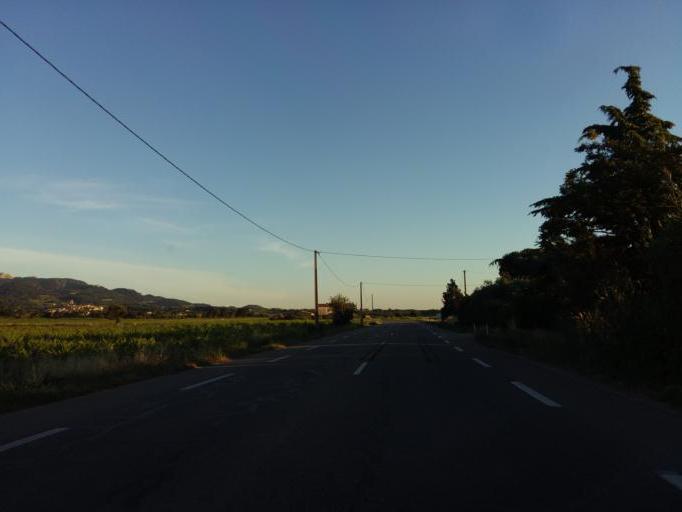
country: FR
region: Provence-Alpes-Cote d'Azur
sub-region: Departement du Vaucluse
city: Sablet
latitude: 44.2100
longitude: 5.0027
